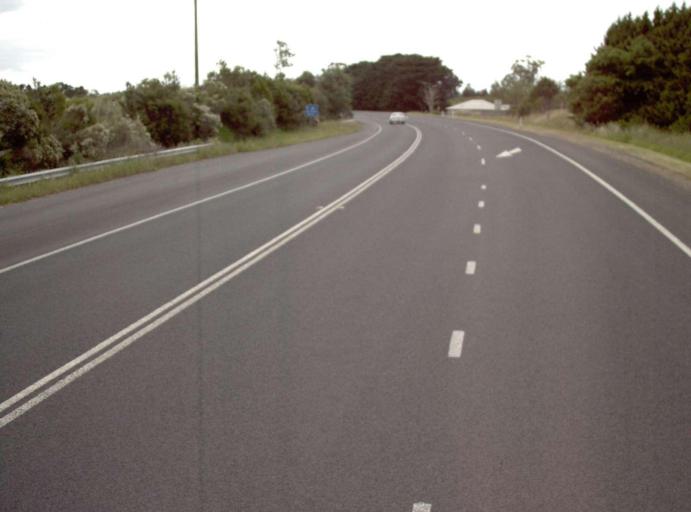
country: AU
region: Victoria
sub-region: Bass Coast
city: North Wonthaggi
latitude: -38.3921
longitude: 145.7488
